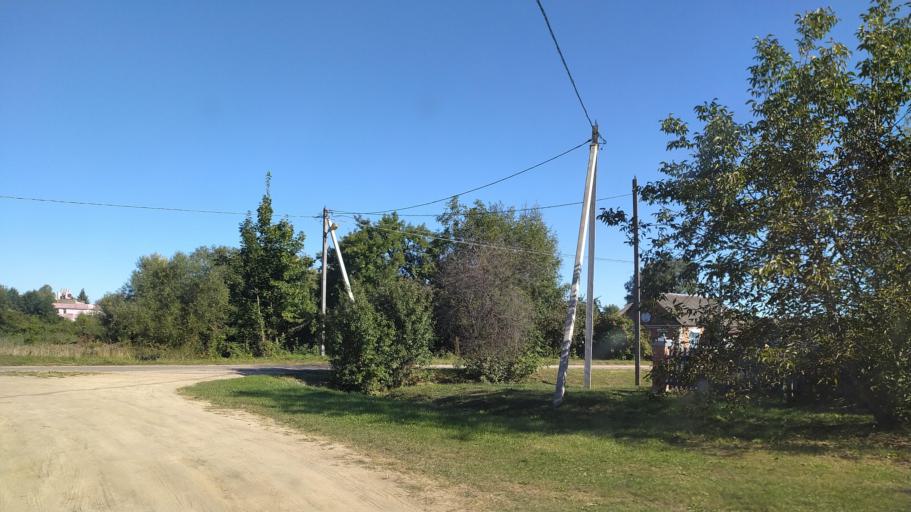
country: BY
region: Brest
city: Pruzhany
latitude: 52.4850
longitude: 24.7096
